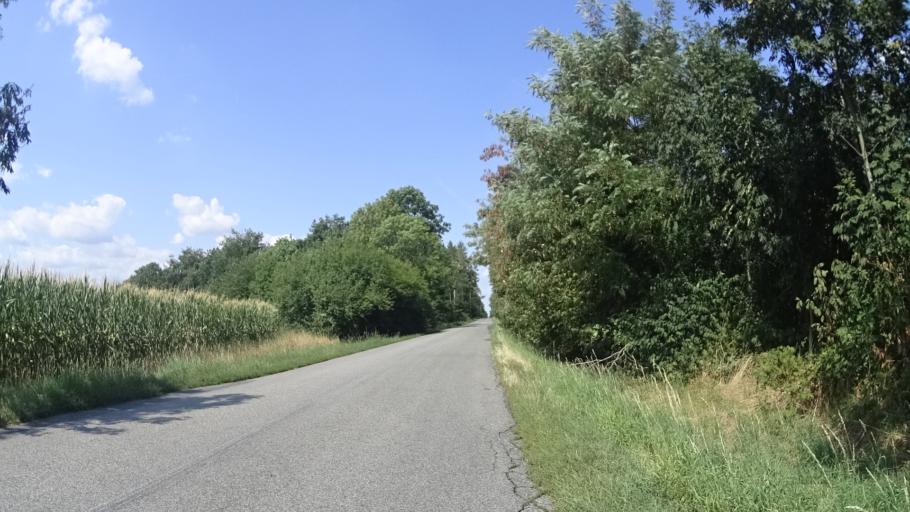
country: CZ
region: Kralovehradecky
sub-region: Okres Jicin
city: Jicin
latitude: 50.3692
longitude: 15.3585
